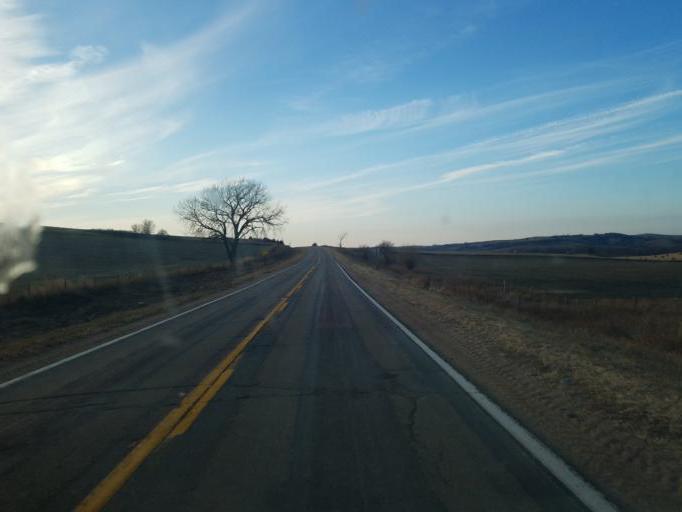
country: US
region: Nebraska
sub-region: Cedar County
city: Hartington
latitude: 42.7321
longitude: -97.2031
